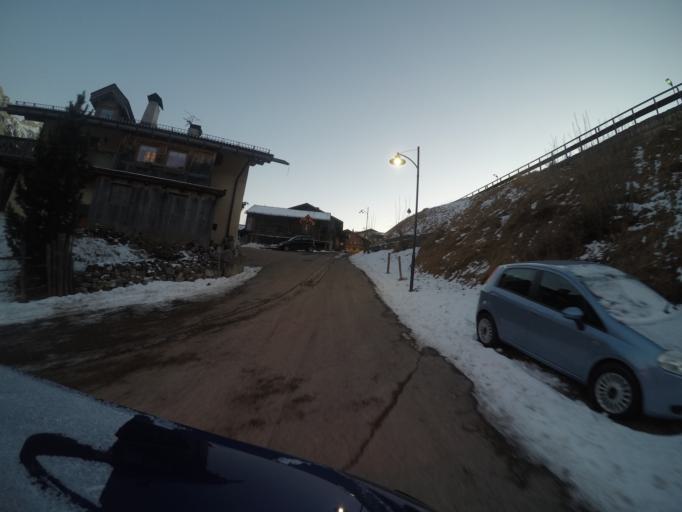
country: IT
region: Trentino-Alto Adige
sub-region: Provincia di Trento
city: Vigo di Fassa
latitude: 46.4173
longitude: 11.6701
